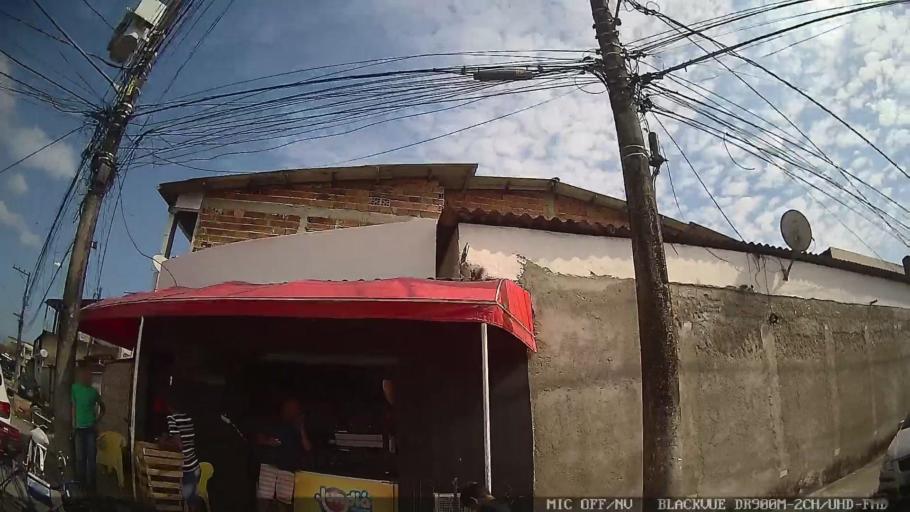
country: BR
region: Sao Paulo
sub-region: Santos
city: Santos
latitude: -23.9521
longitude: -46.2990
